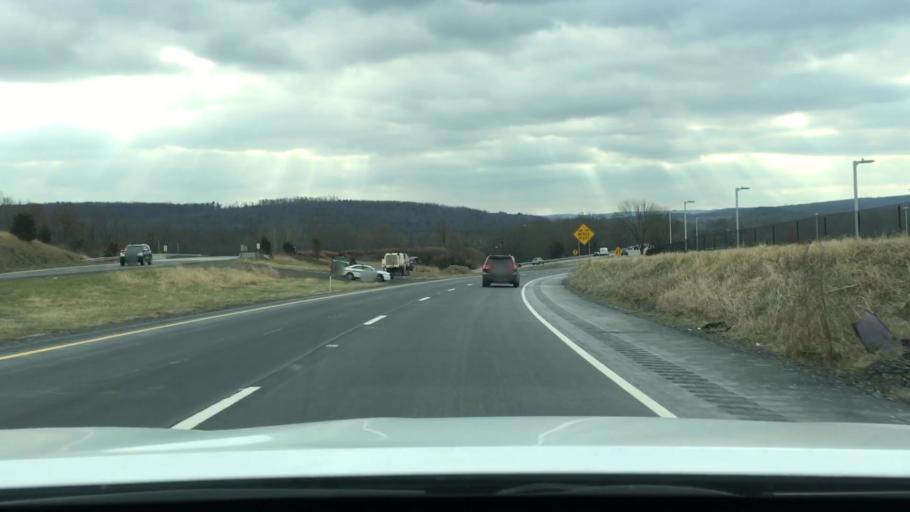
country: US
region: Pennsylvania
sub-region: Monroe County
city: Arlington Heights
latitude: 40.9606
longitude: -75.2844
